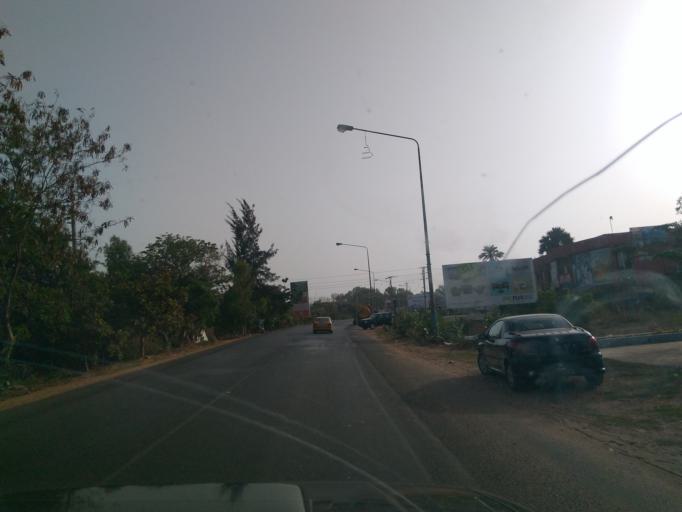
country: GM
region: Banjul
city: Bakau
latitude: 13.4584
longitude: -16.6976
